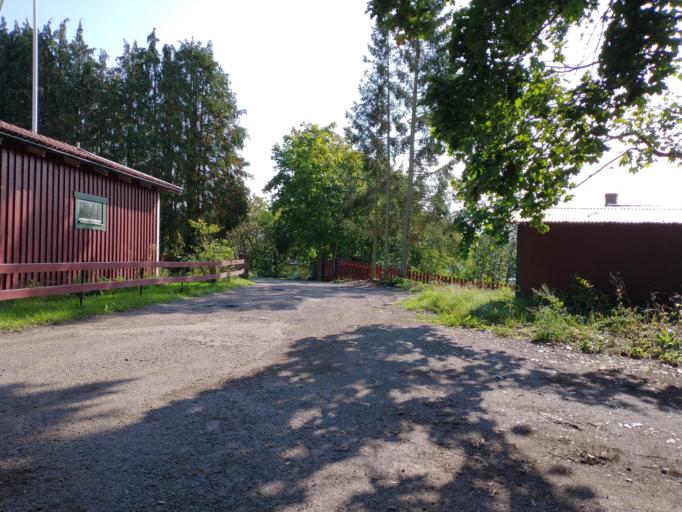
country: SE
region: Kalmar
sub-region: Kalmar Kommun
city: Lindsdal
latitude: 56.7837
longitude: 16.2888
